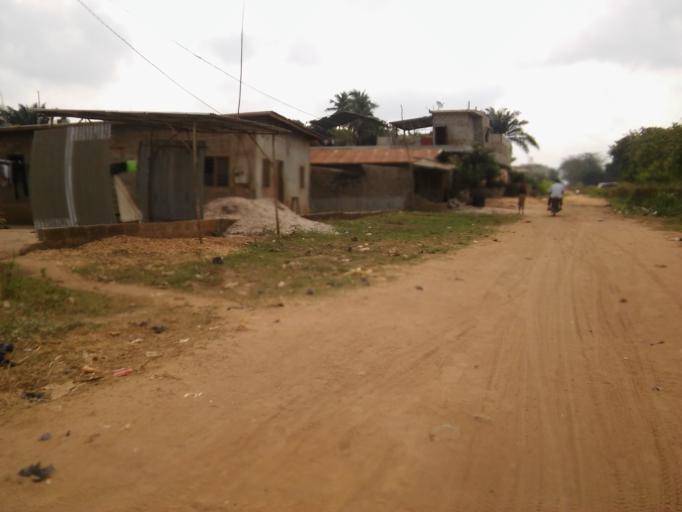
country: BJ
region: Atlantique
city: Abomey-Calavi
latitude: 6.4242
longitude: 2.3277
